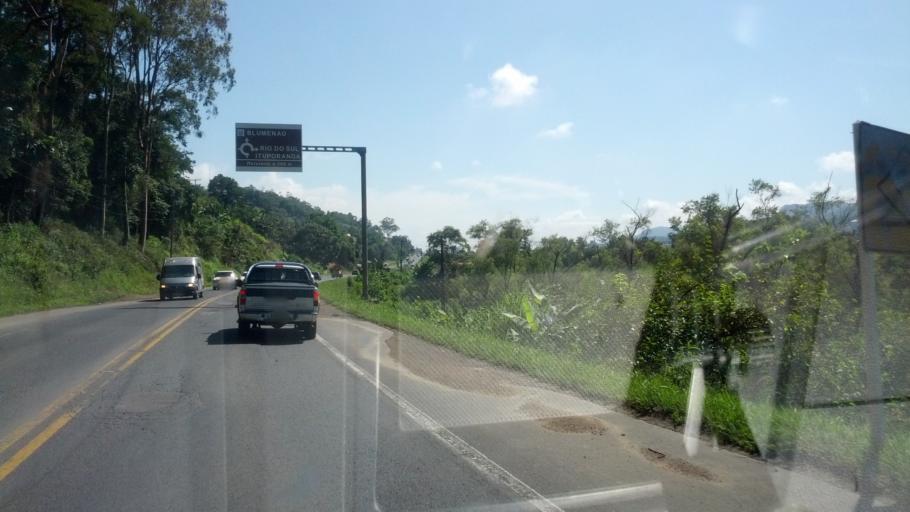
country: BR
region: Santa Catarina
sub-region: Rio Do Sul
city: Rio do Sul
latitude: -27.2233
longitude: -49.6638
